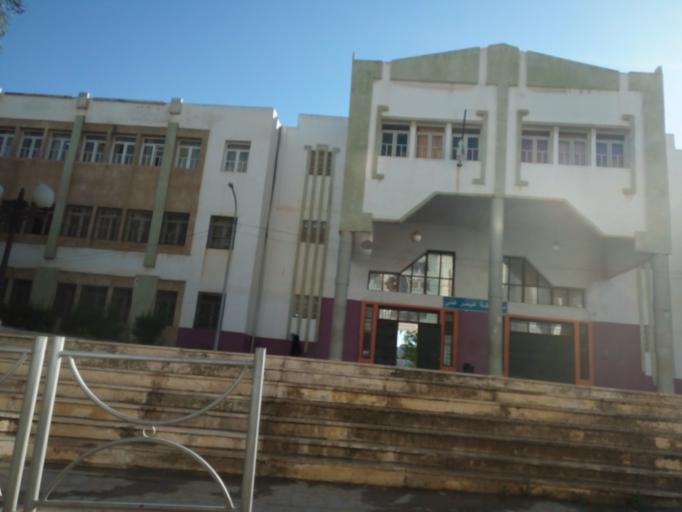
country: DZ
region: Tipaza
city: Saoula
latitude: 36.7289
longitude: 3.0041
